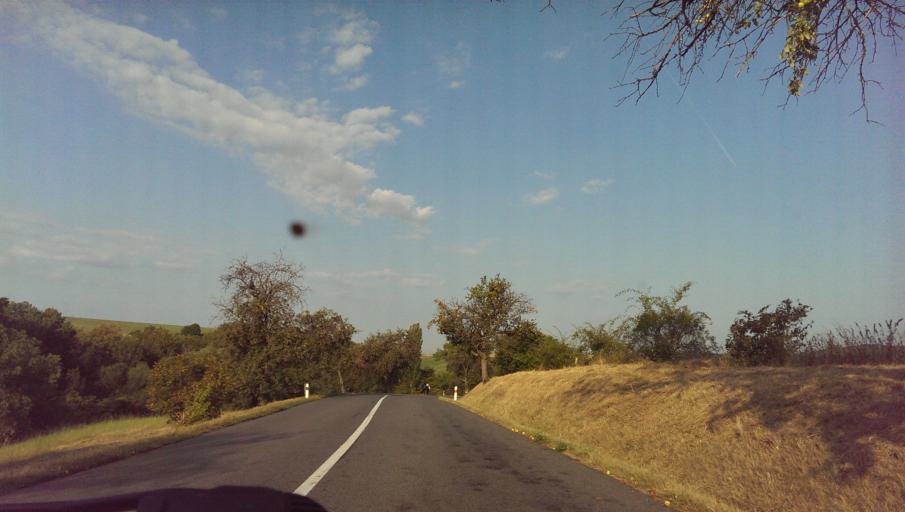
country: CZ
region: South Moravian
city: Zeravice
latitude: 49.0537
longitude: 17.2653
